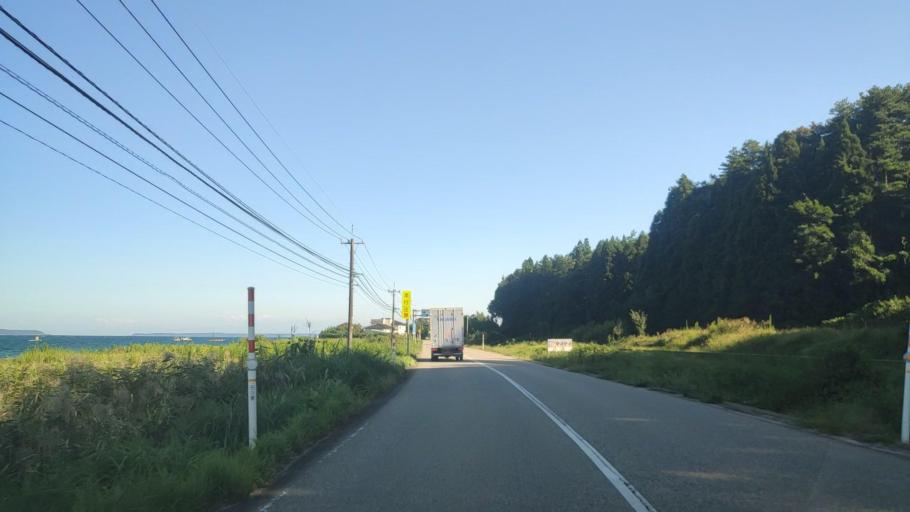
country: JP
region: Ishikawa
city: Nanao
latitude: 37.2007
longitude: 136.9068
